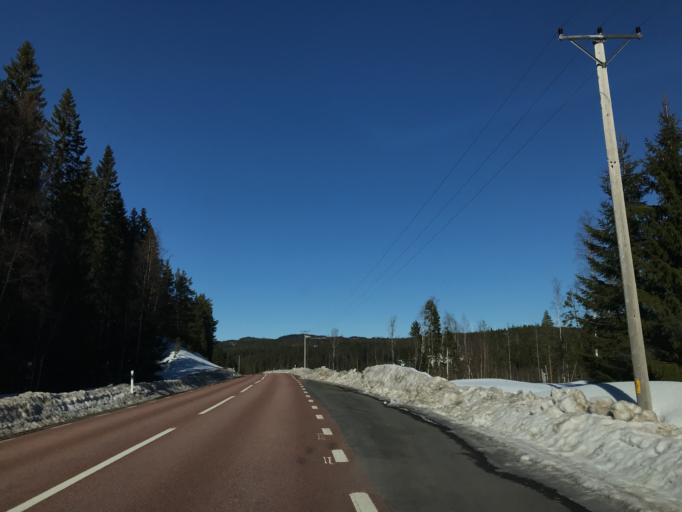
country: SE
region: Vaermland
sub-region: Filipstads Kommun
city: Lesjofors
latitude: 60.2409
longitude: 14.1810
